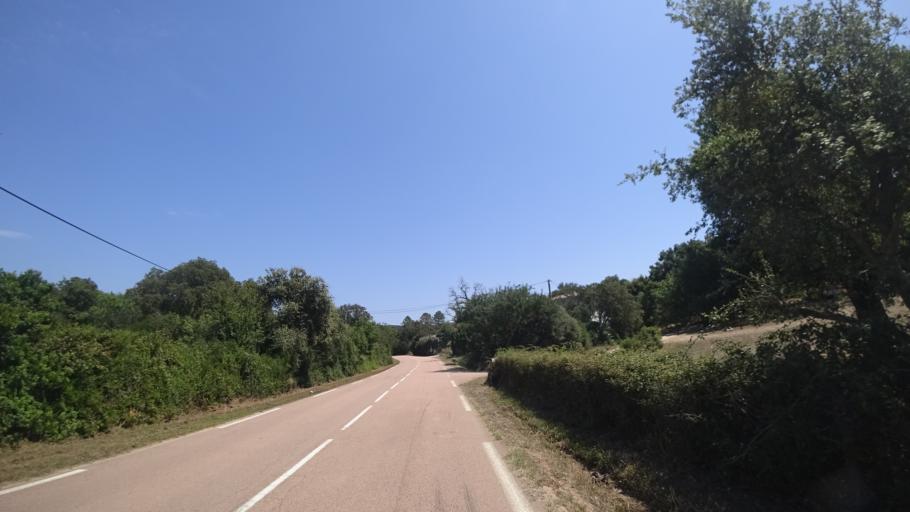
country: FR
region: Corsica
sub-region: Departement de la Corse-du-Sud
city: Porto-Vecchio
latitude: 41.6278
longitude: 9.2484
